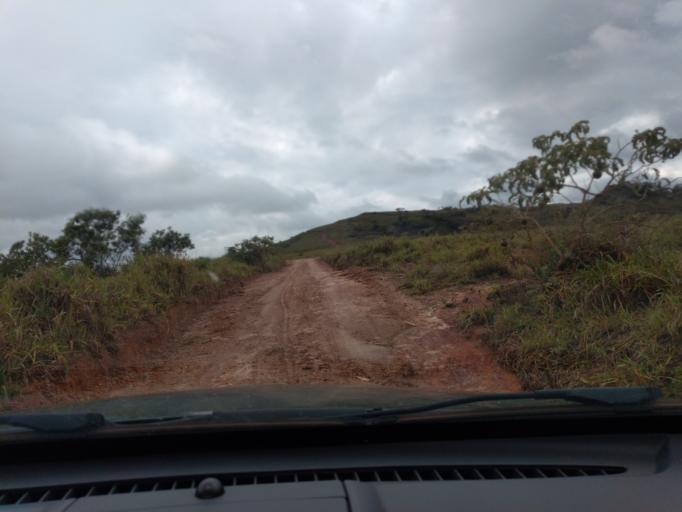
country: BR
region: Minas Gerais
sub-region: Lavras
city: Lavras
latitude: -21.5145
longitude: -44.9294
